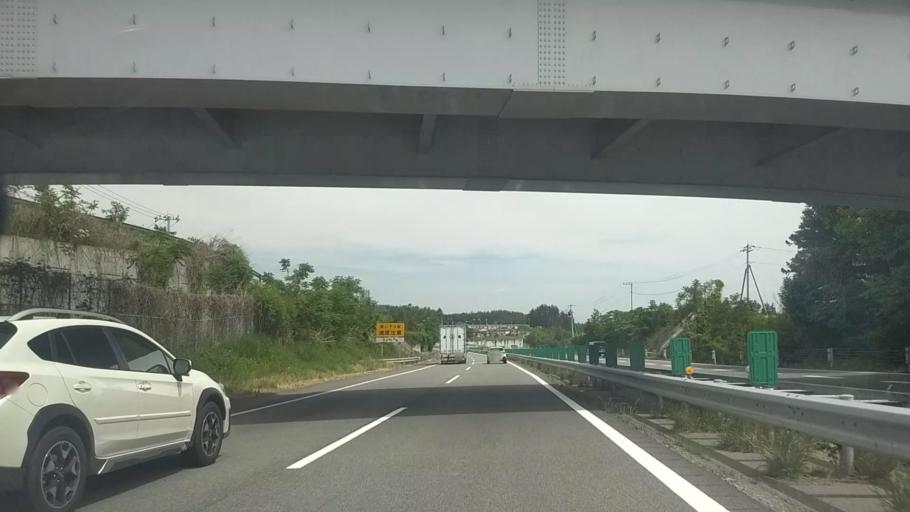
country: JP
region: Yamanashi
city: Nirasaki
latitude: 35.8479
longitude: 138.3589
